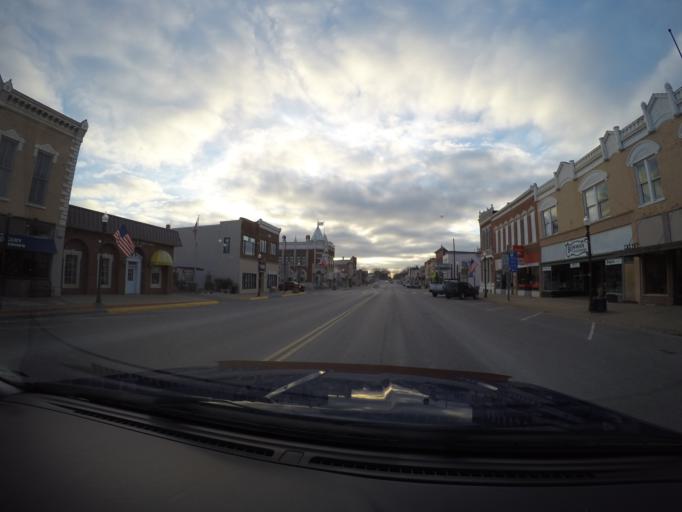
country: US
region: Kansas
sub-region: Morris County
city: Council Grove
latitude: 38.6612
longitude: -96.4900
